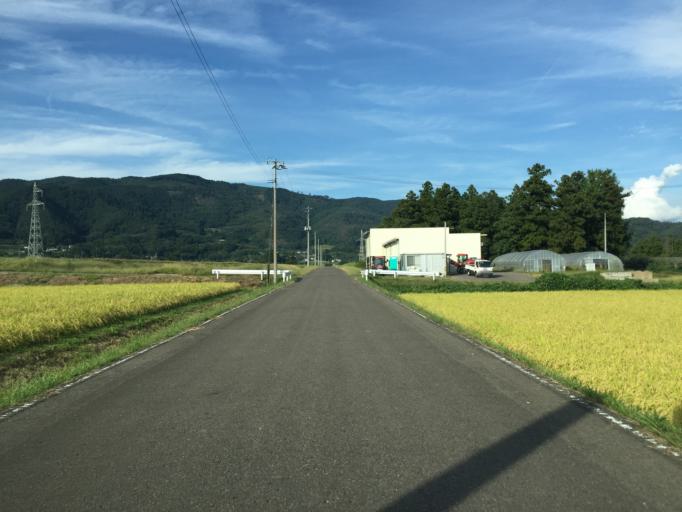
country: JP
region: Fukushima
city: Hobaramachi
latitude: 37.8804
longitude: 140.5243
